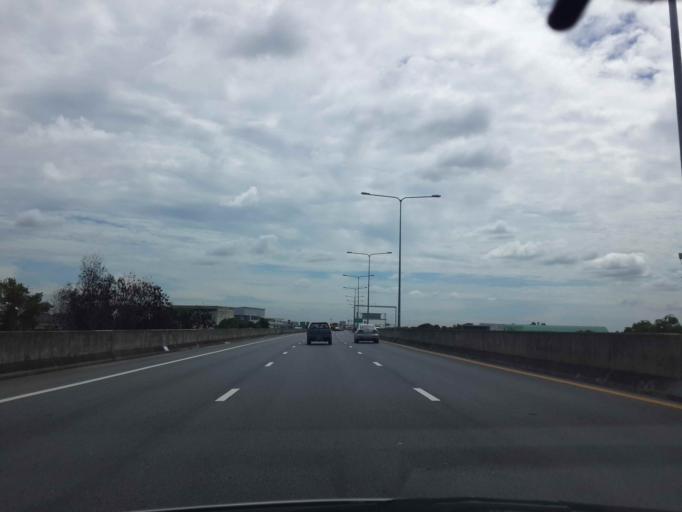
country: TH
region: Bangkok
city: Sai Mai
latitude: 13.8954
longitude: 100.6655
